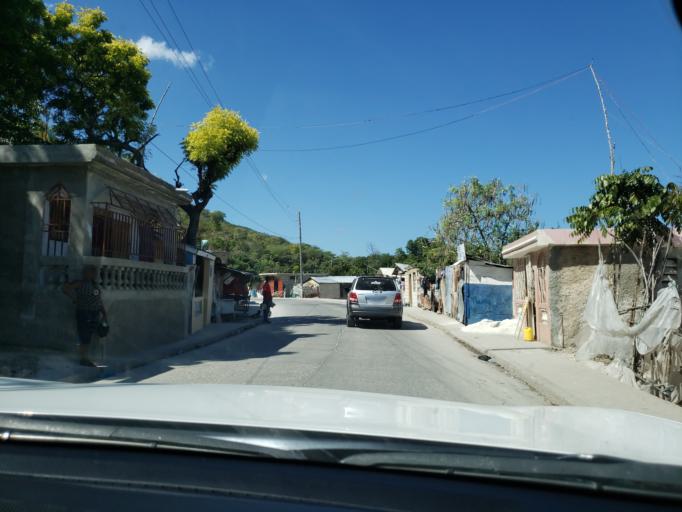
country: HT
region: Nippes
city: Miragoane
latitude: 18.4438
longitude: -73.0967
